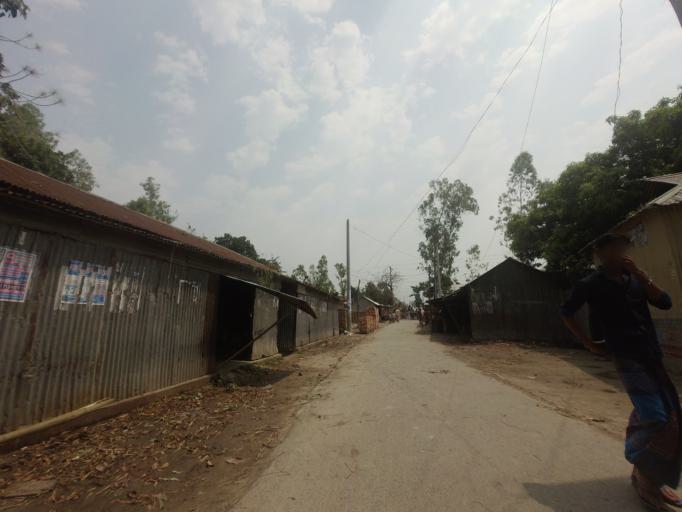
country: BD
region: Rajshahi
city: Sirajganj
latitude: 24.3273
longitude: 89.6984
